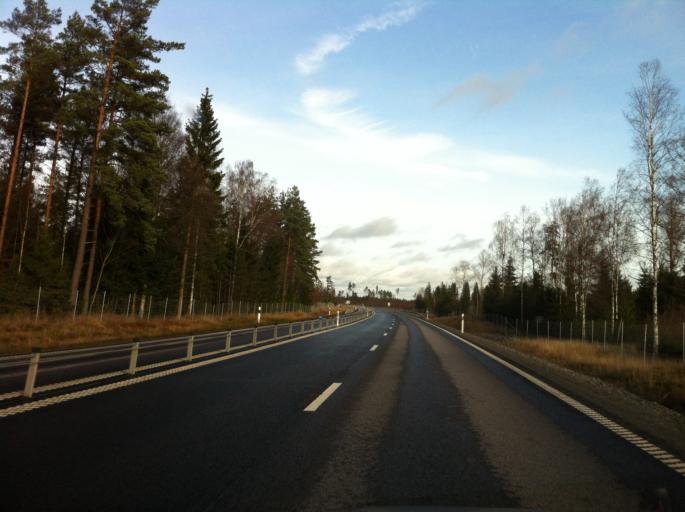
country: SE
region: Kronoberg
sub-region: Almhults Kommun
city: AElmhult
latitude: 56.6272
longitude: 14.2529
